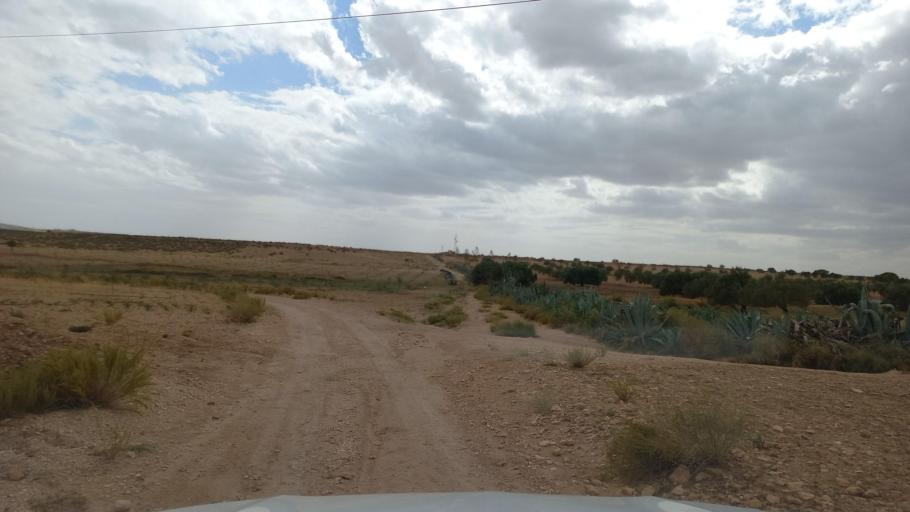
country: TN
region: Al Qasrayn
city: Sbiba
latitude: 35.3843
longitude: 9.1045
